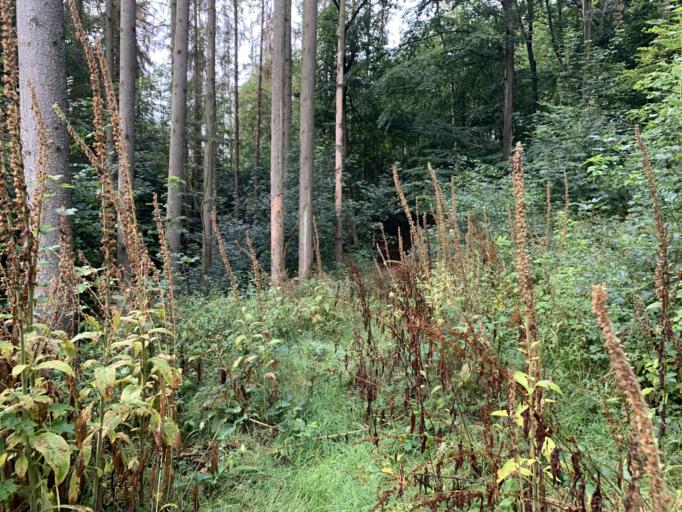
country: DE
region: Rheinland-Pfalz
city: Holzhausen an der Haide
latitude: 50.2193
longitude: 7.9213
